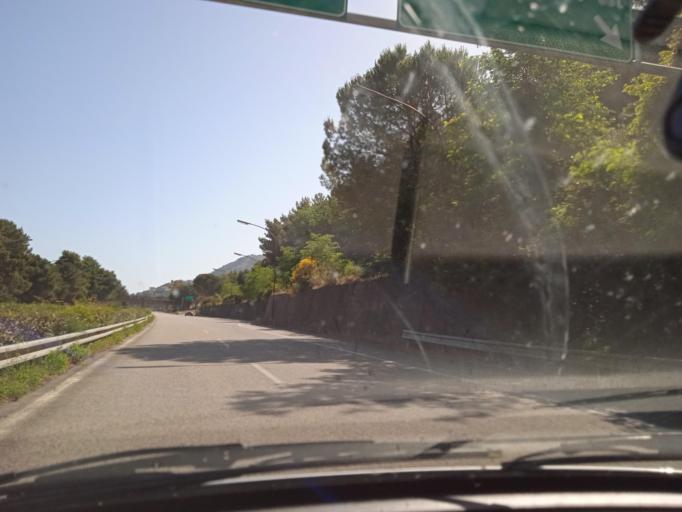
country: IT
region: Sicily
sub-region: Messina
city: Brolo
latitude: 38.1454
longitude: 14.8242
